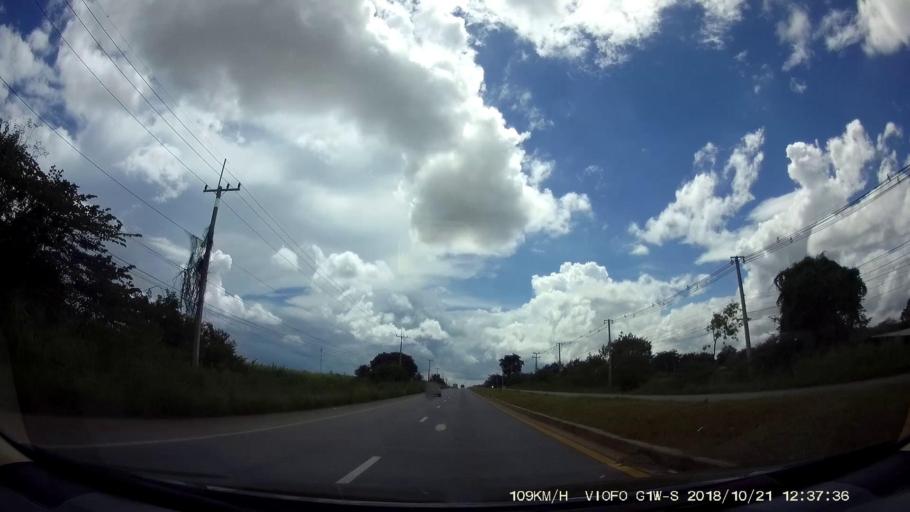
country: TH
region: Nakhon Ratchasima
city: Dan Khun Thot
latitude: 15.0666
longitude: 101.7105
